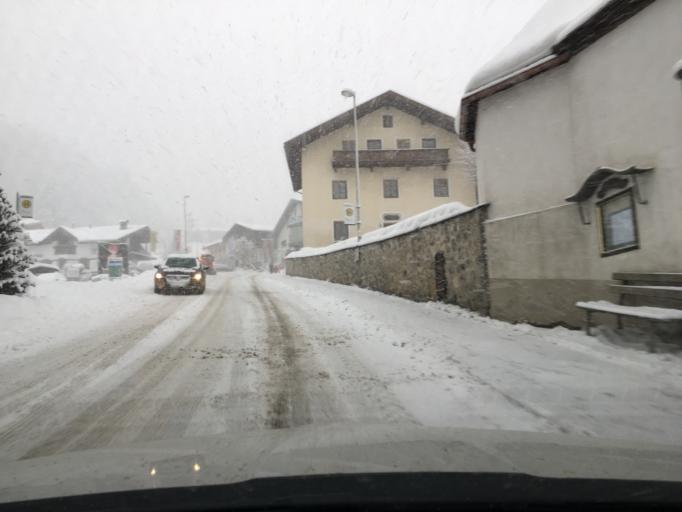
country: AT
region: Tyrol
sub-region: Politischer Bezirk Schwaz
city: Mayrhofen
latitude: 47.1542
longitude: 11.8249
